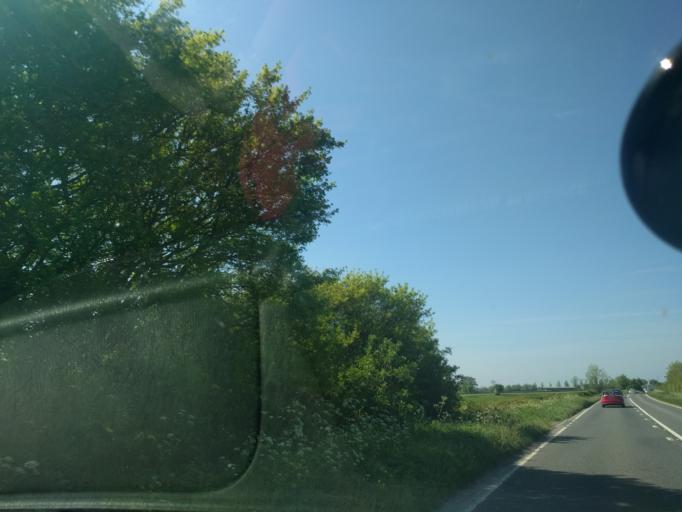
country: GB
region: England
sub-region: Somerset
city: Ilchester
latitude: 51.0675
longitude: -2.6279
